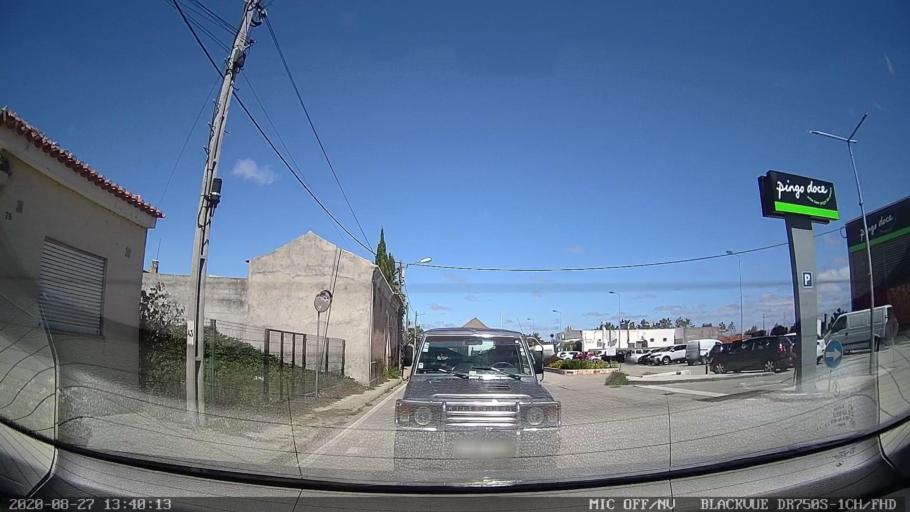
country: PT
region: Coimbra
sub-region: Mira
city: Mira
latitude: 40.4359
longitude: -8.7285
